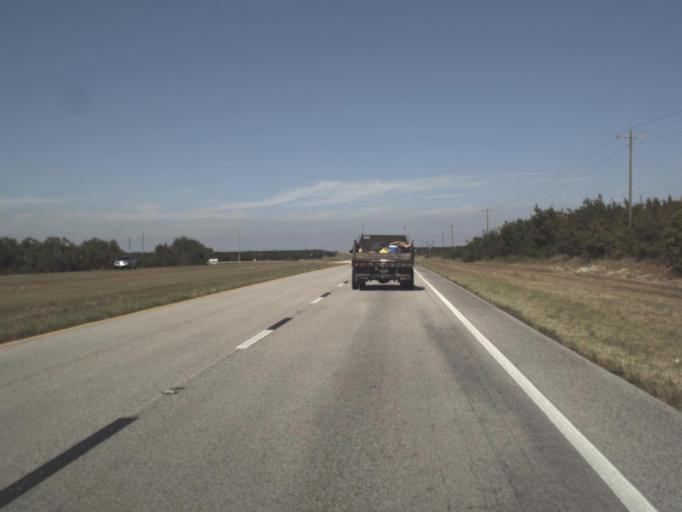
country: US
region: Florida
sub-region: Highlands County
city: Placid Lakes
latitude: 27.1320
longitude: -81.3295
